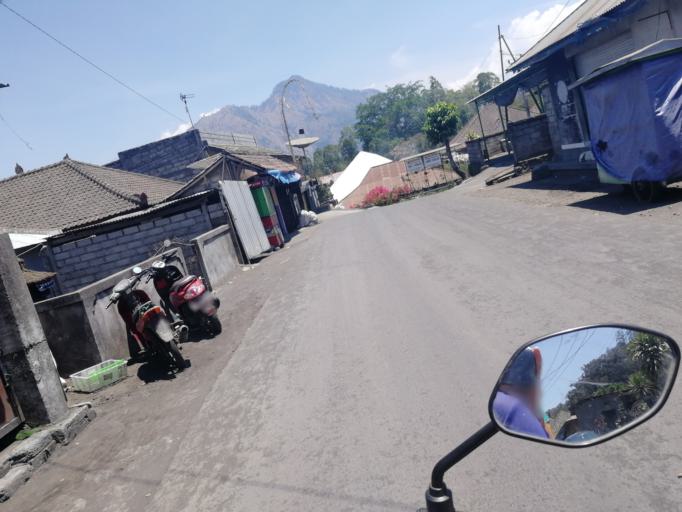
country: ID
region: Bali
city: Banjar Trunyan
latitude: -8.2280
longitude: 115.4096
